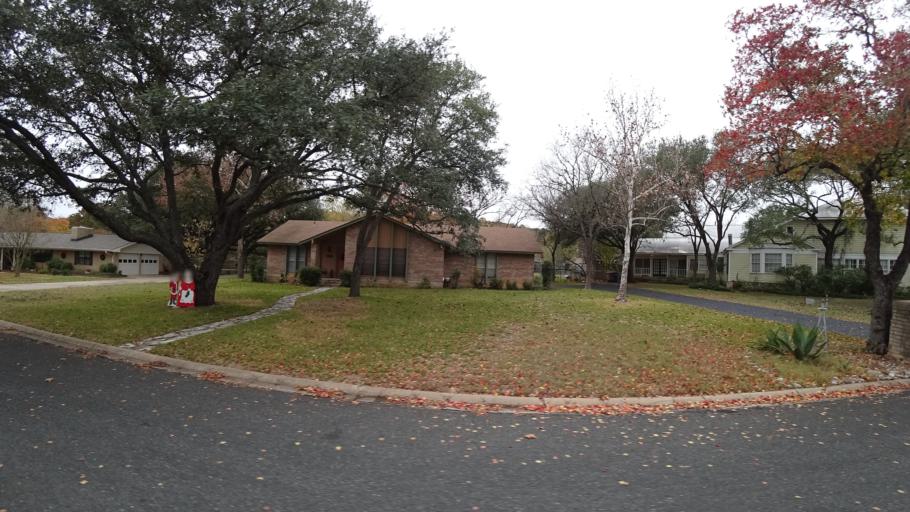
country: US
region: Texas
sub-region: Williamson County
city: Jollyville
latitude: 30.3752
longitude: -97.7854
